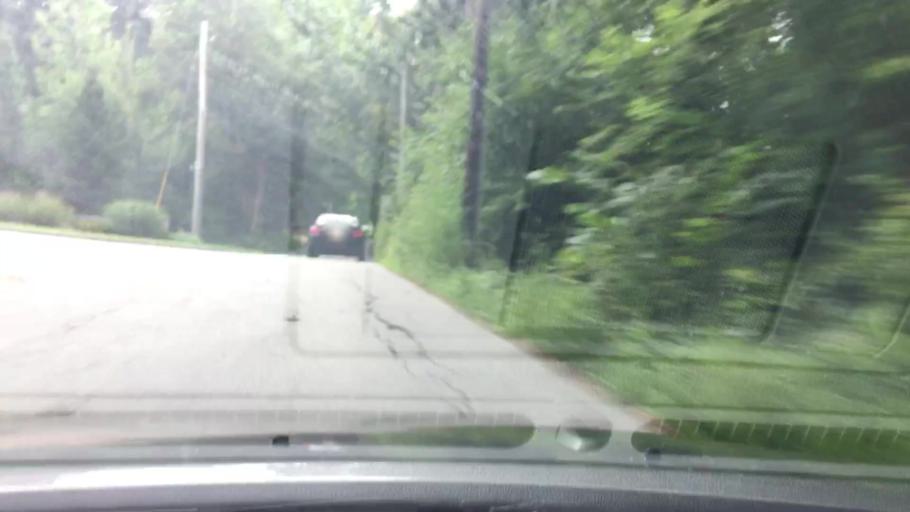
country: US
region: Rhode Island
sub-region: Providence County
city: Cumberland Hill
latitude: 42.0280
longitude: -71.4568
